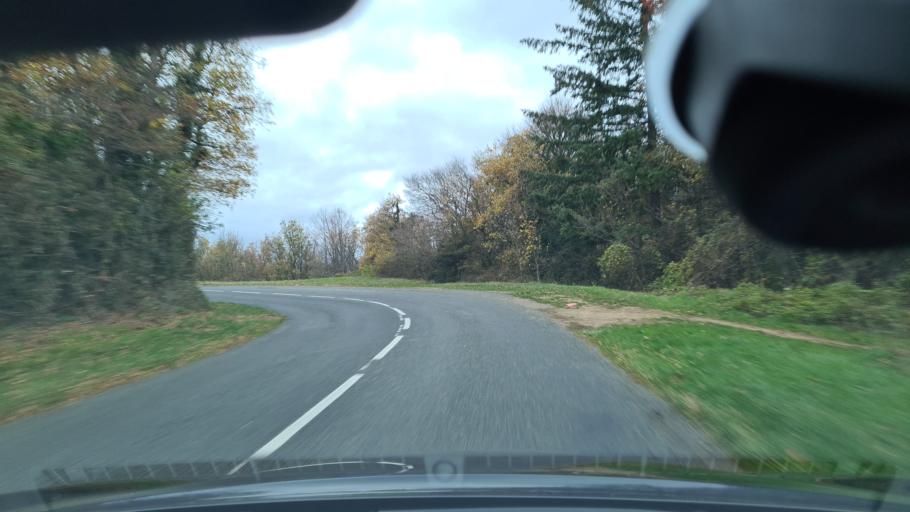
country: FR
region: Rhone-Alpes
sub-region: Departement du Rhone
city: Limonest
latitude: 45.8417
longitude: 4.7895
